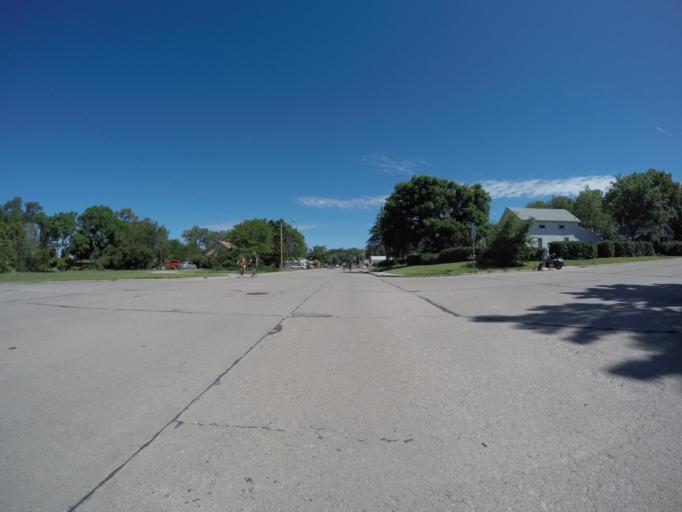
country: US
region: Kansas
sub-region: Rawlins County
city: Atwood
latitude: 39.8112
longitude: -101.0423
